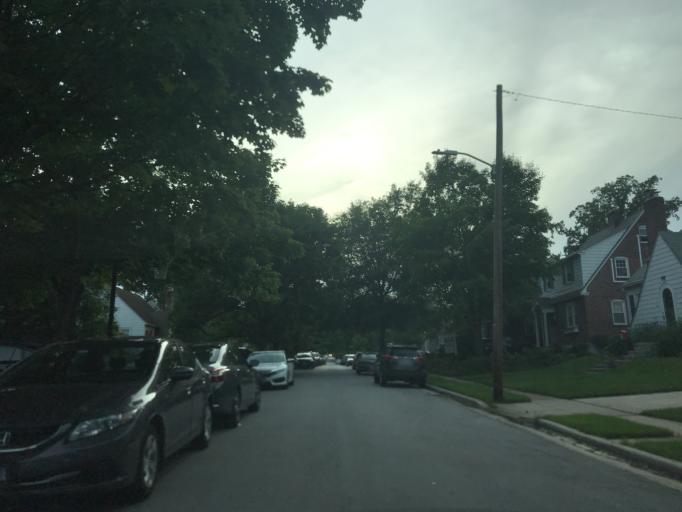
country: US
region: Maryland
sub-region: Baltimore County
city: Towson
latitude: 39.3753
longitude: -76.5990
